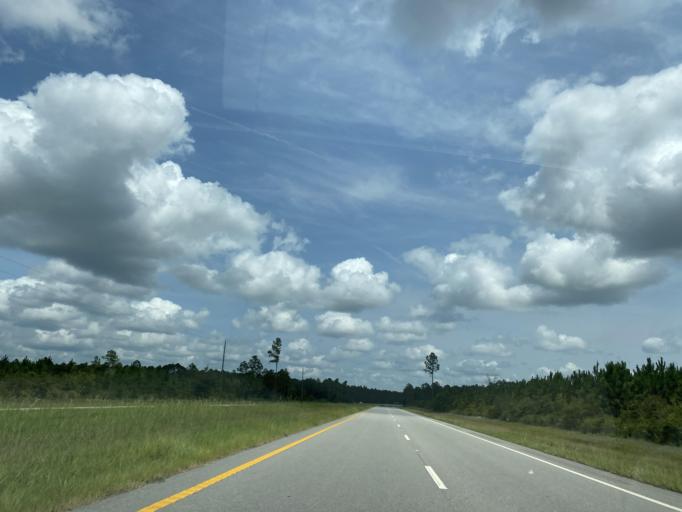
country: US
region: Georgia
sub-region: Ware County
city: Deenwood
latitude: 31.2726
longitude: -82.4419
